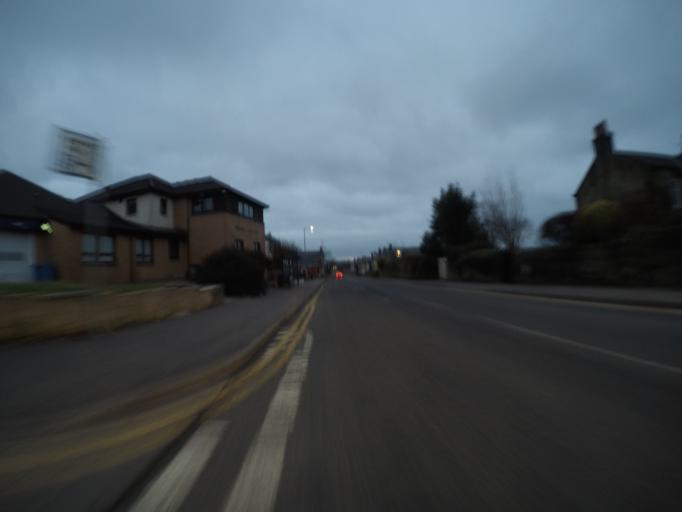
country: GB
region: Scotland
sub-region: North Ayrshire
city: Kilwinning
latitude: 55.6529
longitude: -4.7010
